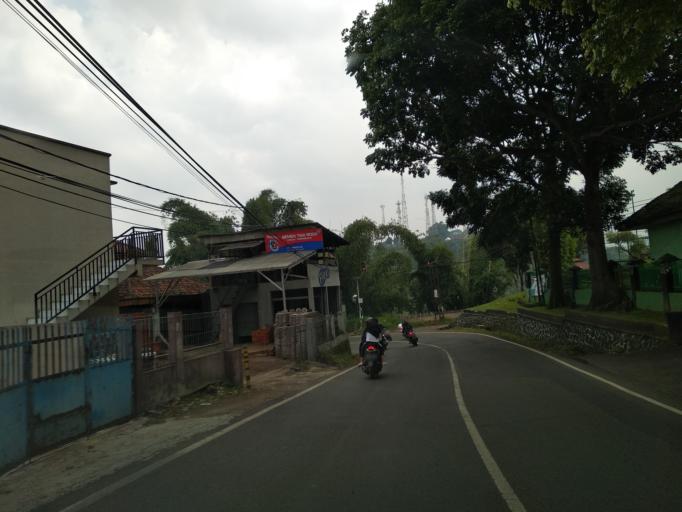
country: ID
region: West Java
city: Lembang
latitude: -6.8254
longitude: 107.6088
